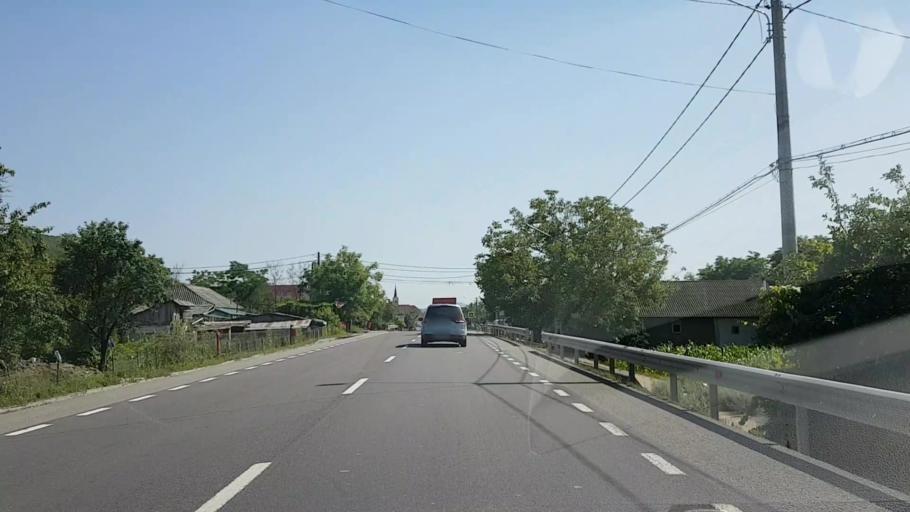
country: RO
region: Bistrita-Nasaud
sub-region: Comuna Sieu-Odorhei
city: Sieu-Odorhei
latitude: 47.1516
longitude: 24.3059
